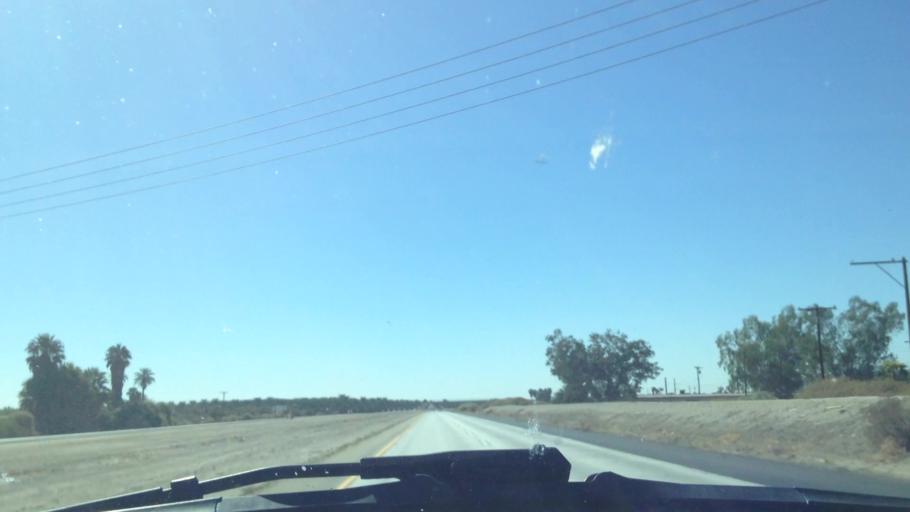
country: US
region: California
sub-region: Riverside County
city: Thermal
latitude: 33.6345
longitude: -116.1281
